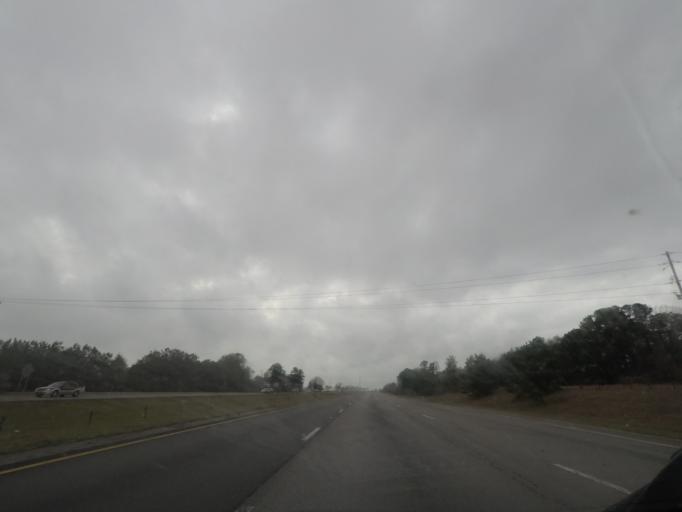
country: US
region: South Carolina
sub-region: Orangeburg County
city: Holly Hill
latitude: 33.5210
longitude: -80.4324
